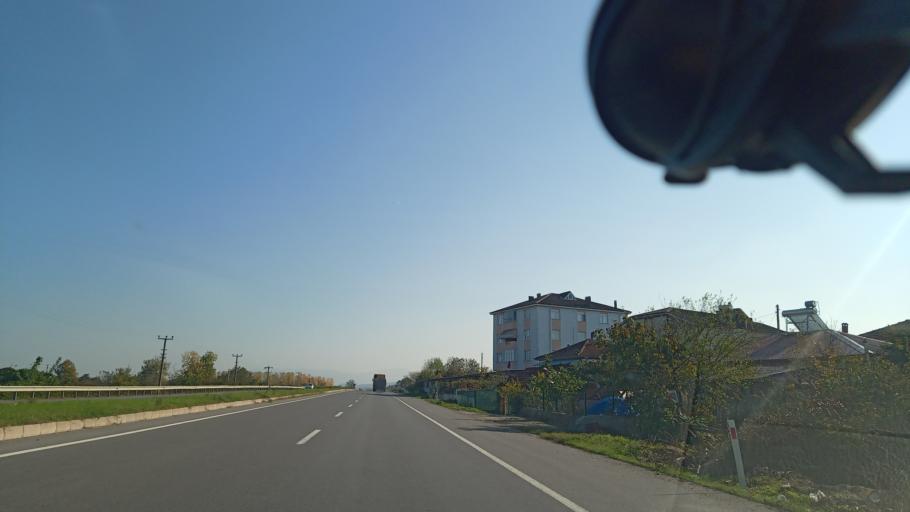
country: TR
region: Sakarya
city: Karasu
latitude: 41.0741
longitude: 30.7859
